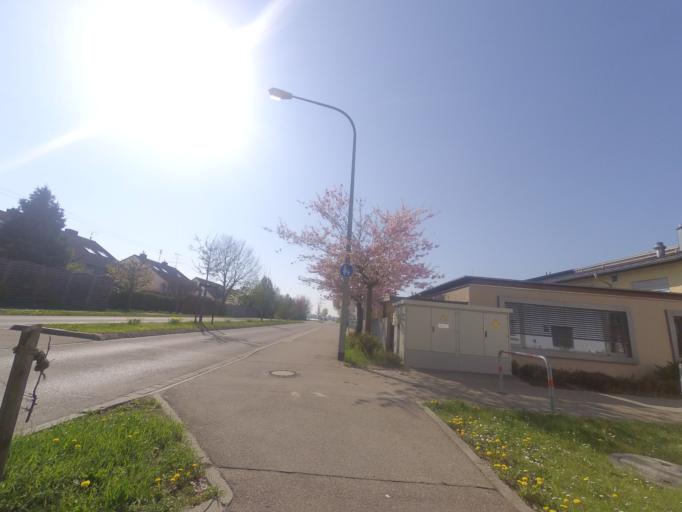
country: DE
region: Bavaria
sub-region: Swabia
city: Nersingen
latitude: 48.4263
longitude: 10.1257
